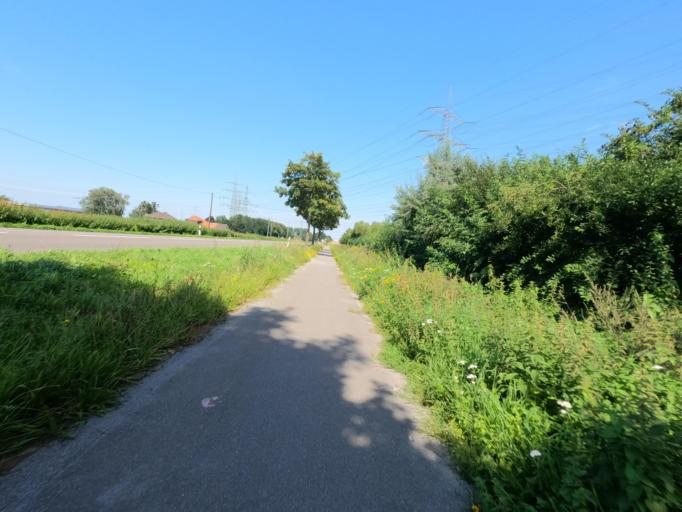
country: DE
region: North Rhine-Westphalia
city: Baesweiler
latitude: 50.9394
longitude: 6.2139
